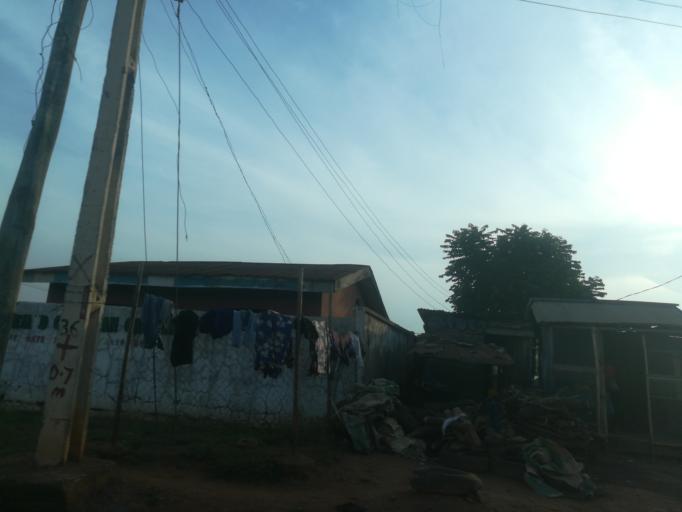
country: NG
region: Oyo
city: Moniya
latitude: 7.5357
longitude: 3.9037
